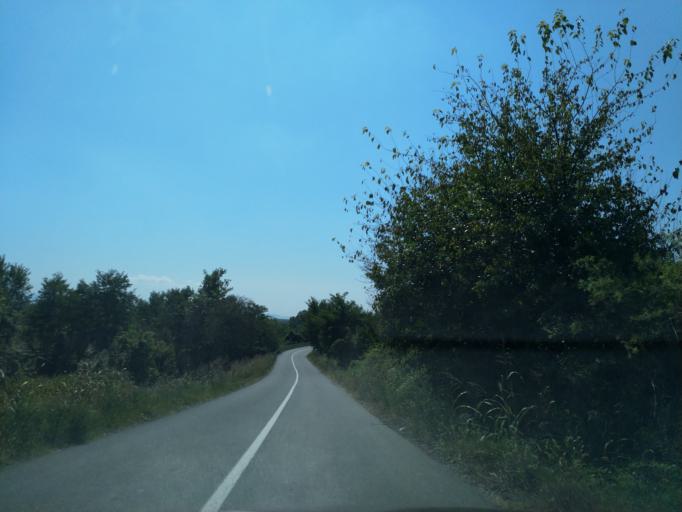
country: RS
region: Central Serbia
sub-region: Rasinski Okrug
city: Krusevac
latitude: 43.6307
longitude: 21.3722
